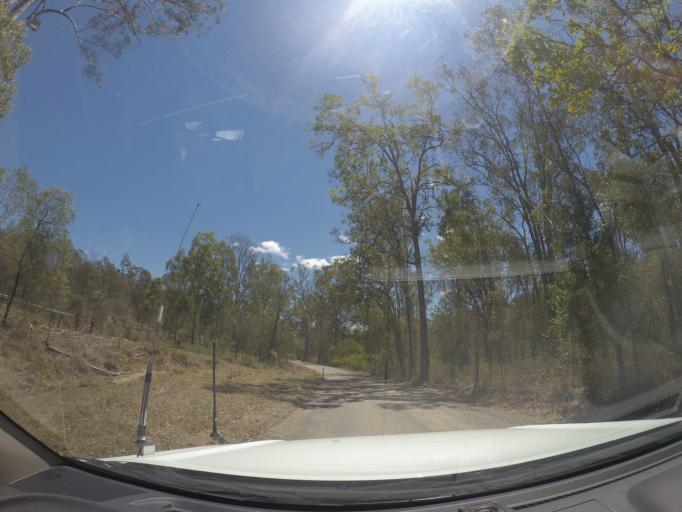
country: AU
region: Queensland
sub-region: Ipswich
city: Redbank Plains
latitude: -27.7579
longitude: 152.8367
